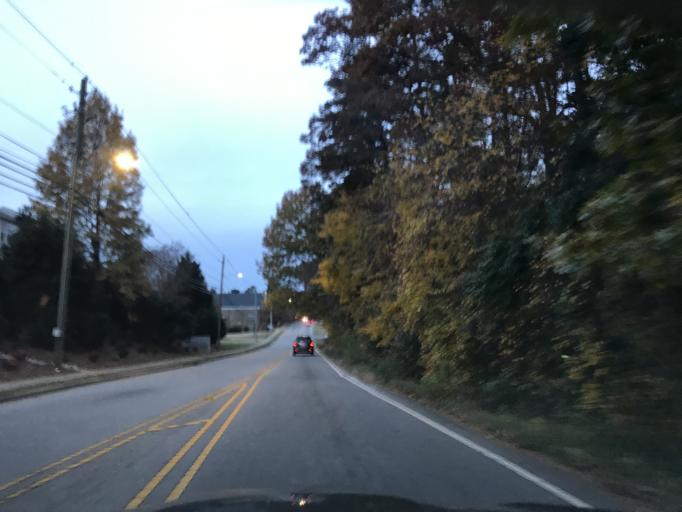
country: US
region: North Carolina
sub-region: Wake County
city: Raleigh
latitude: 35.8472
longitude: -78.6077
